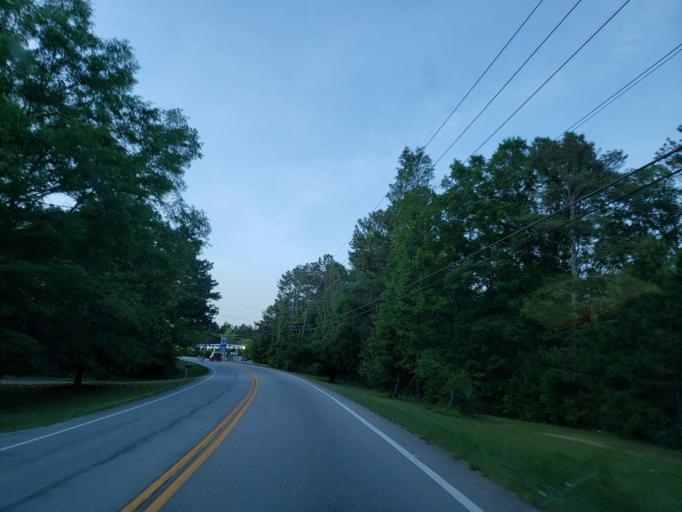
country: US
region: Georgia
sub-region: Douglas County
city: Douglasville
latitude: 33.6669
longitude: -84.8058
